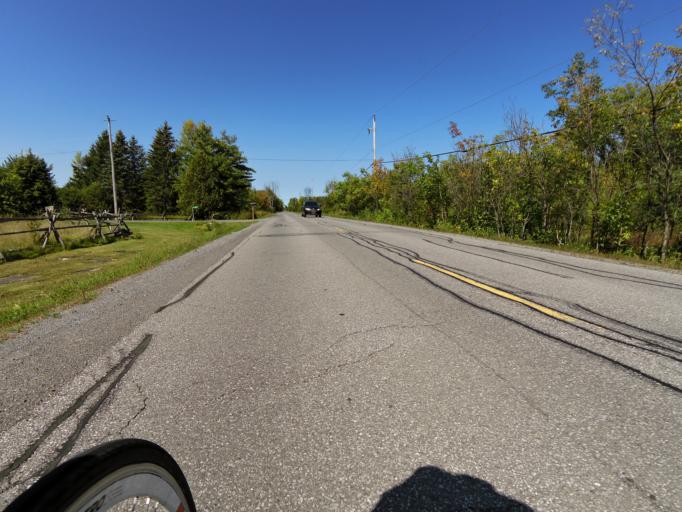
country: CA
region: Ontario
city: Bells Corners
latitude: 45.3915
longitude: -76.0065
